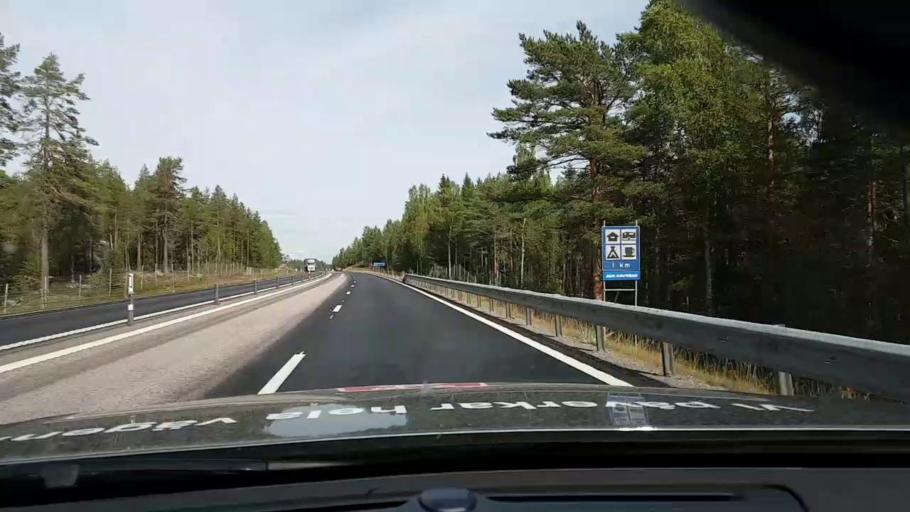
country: SE
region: Vaesternorrland
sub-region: OErnskoeldsviks Kommun
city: Husum
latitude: 63.4730
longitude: 19.2850
